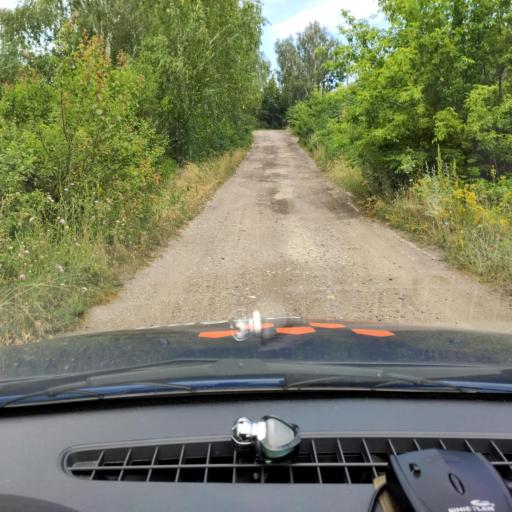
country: RU
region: Voronezj
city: Ramon'
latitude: 52.0754
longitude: 39.3178
